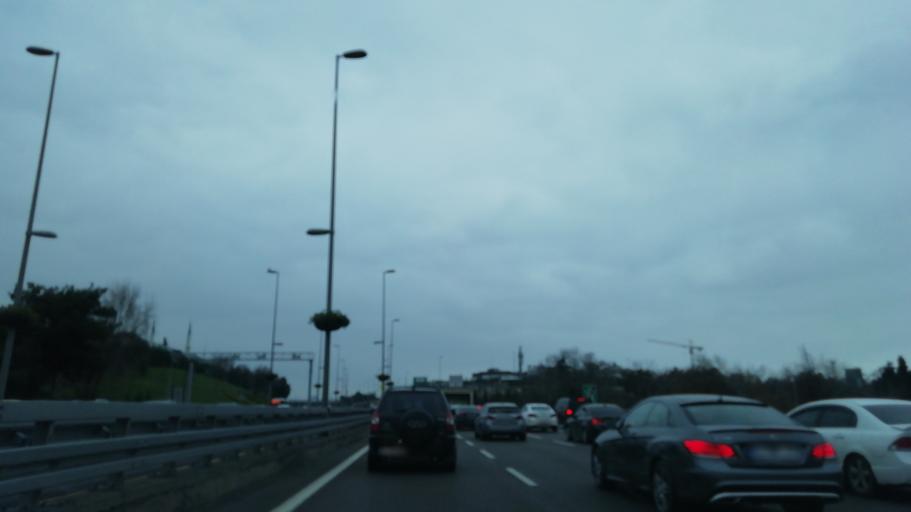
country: TR
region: Istanbul
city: UEskuedar
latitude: 41.0284
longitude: 29.0457
